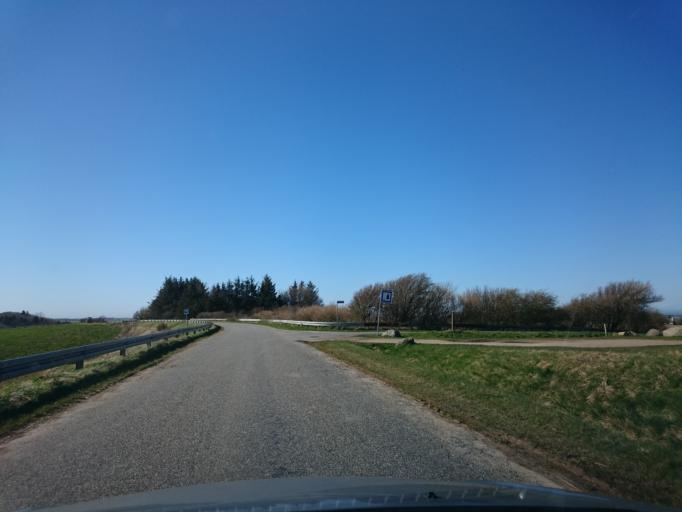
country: DK
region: North Denmark
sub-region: Hjorring Kommune
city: Hjorring
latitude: 57.5340
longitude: 10.0372
